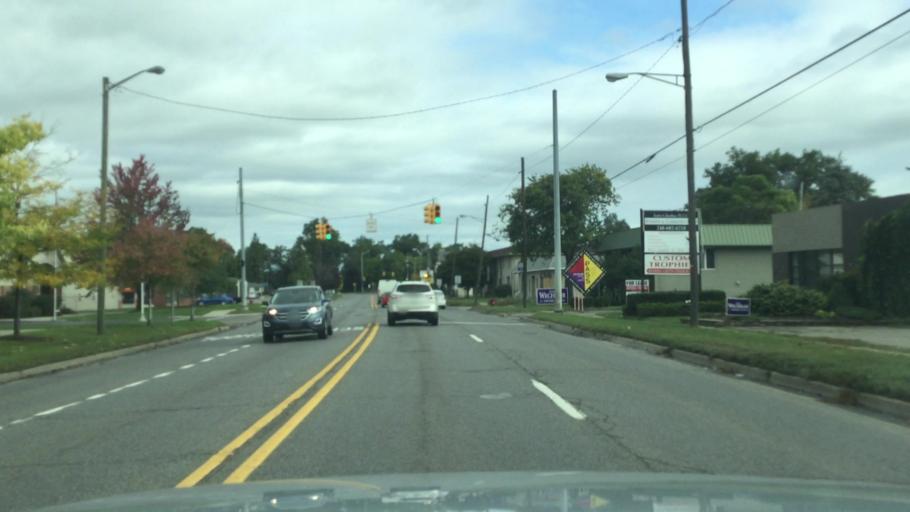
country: US
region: Michigan
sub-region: Oakland County
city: Keego Harbor
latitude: 42.6013
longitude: -83.3487
